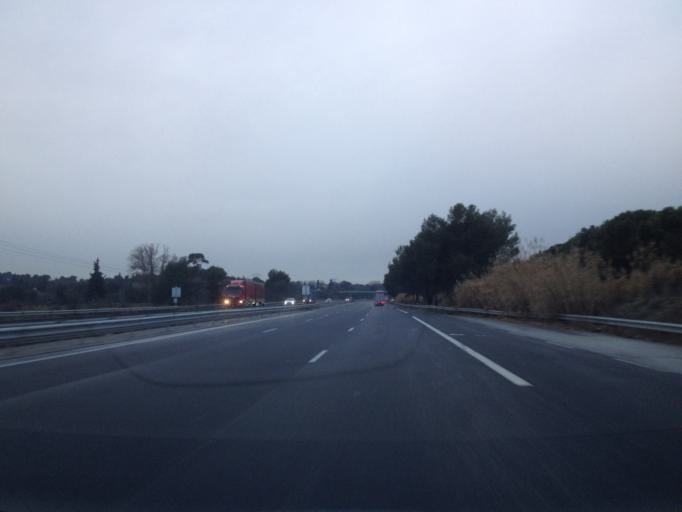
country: FR
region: Provence-Alpes-Cote d'Azur
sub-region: Departement des Bouches-du-Rhone
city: Aix-en-Provence
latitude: 43.5199
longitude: 5.4239
